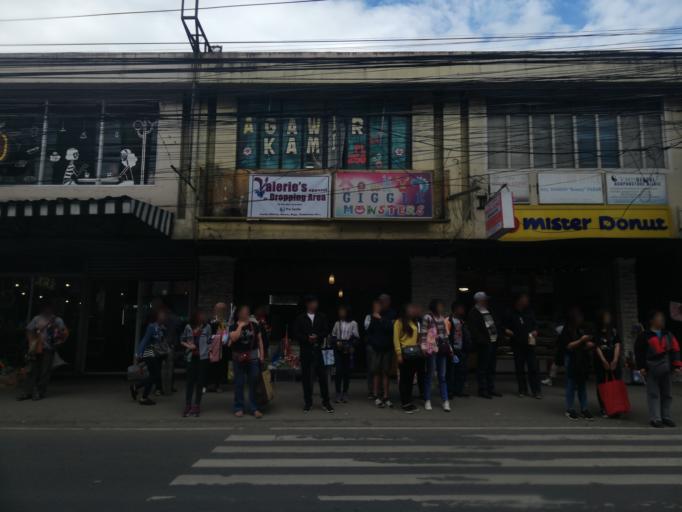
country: PH
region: Cordillera
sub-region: Province of Benguet
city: La Trinidad
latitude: 16.4435
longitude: 120.5922
